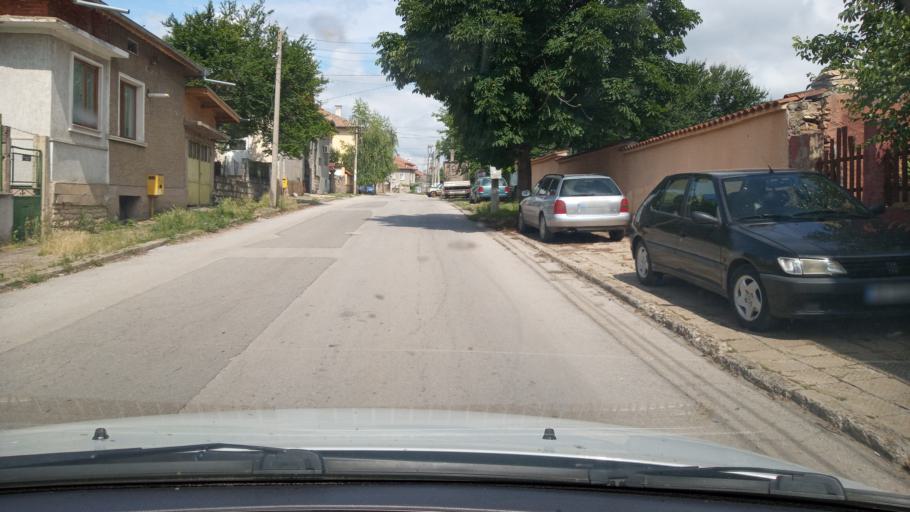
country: BG
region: Lovech
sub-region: Obshtina Lukovit
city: Lukovit
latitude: 43.2068
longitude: 24.1565
